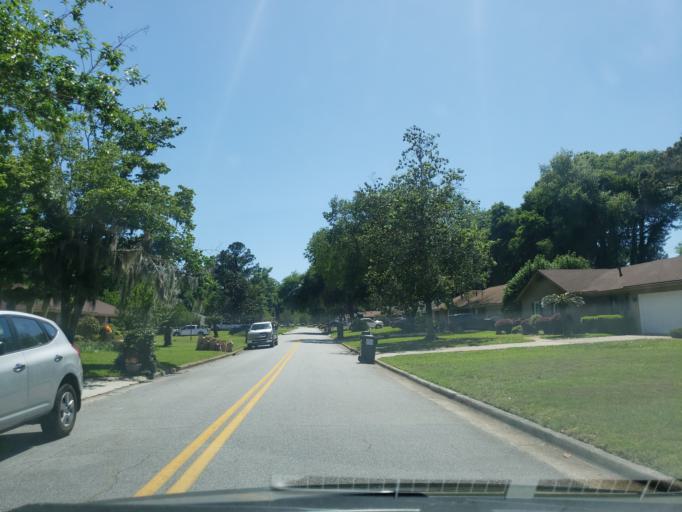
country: US
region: Georgia
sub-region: Chatham County
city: Isle of Hope
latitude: 31.9878
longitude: -81.0932
